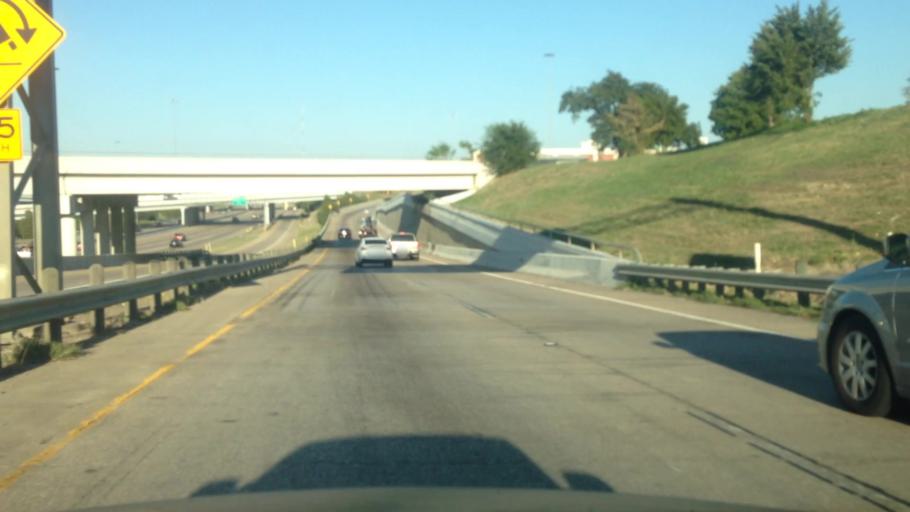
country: US
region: Texas
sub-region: Tarrant County
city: Fort Worth
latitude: 32.7473
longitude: -97.3131
